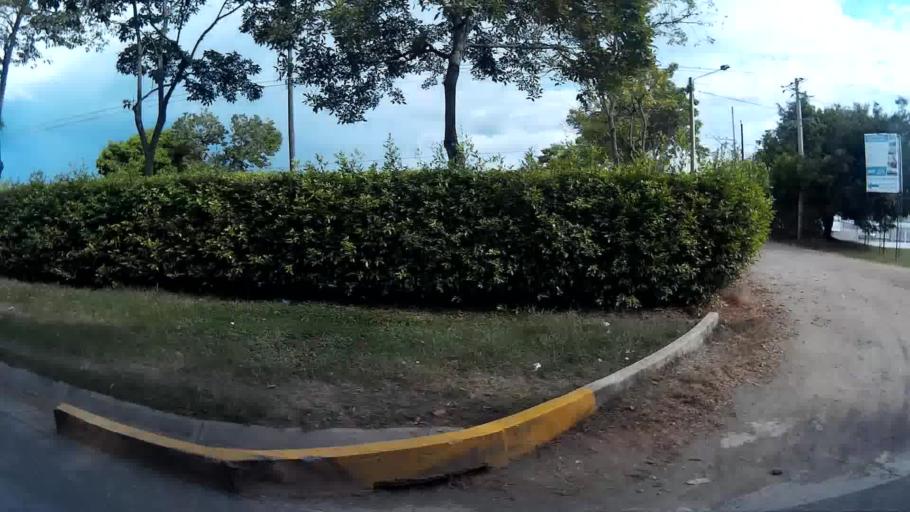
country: CO
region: Valle del Cauca
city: Cartago
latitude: 4.8031
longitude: -75.8323
